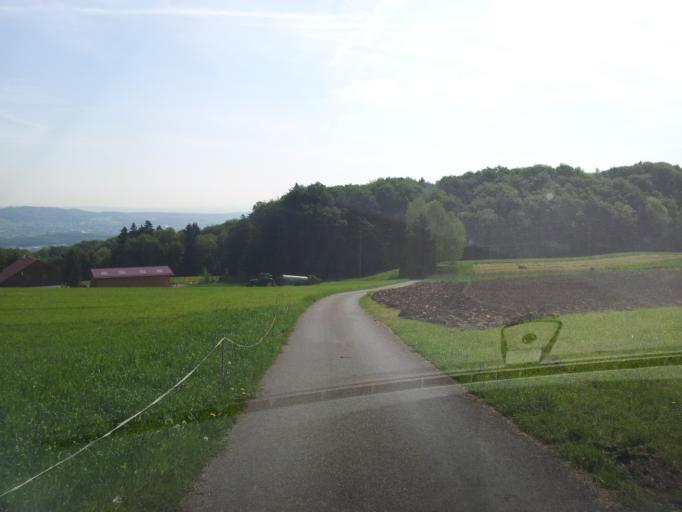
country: CH
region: Aargau
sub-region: Bezirk Bremgarten
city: Rudolfstetten
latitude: 47.3874
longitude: 8.3692
